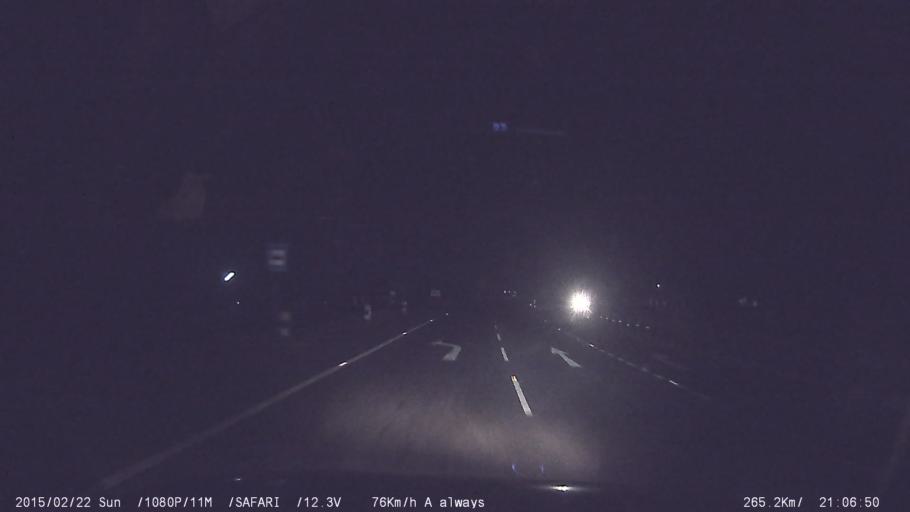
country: IN
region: Tamil Nadu
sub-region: Karur
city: Pallappatti
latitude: 10.7150
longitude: 77.9292
